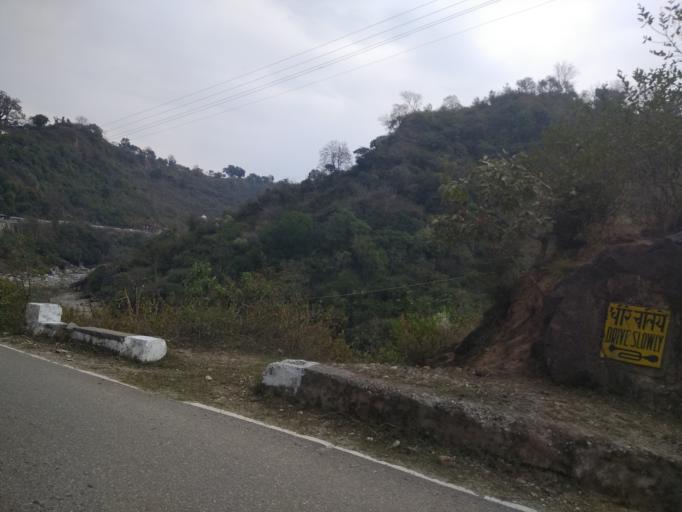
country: IN
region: Himachal Pradesh
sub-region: Kangra
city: Kotla
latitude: 32.2290
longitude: 76.0652
